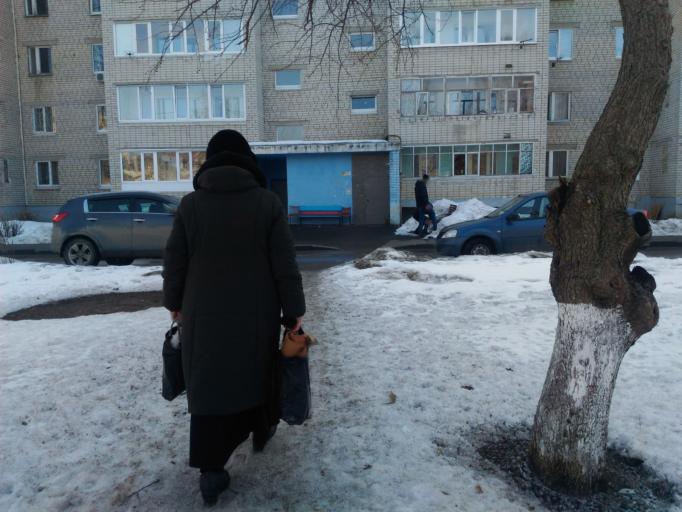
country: RU
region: Ulyanovsk
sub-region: Ulyanovskiy Rayon
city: Ulyanovsk
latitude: 54.3261
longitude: 48.4848
